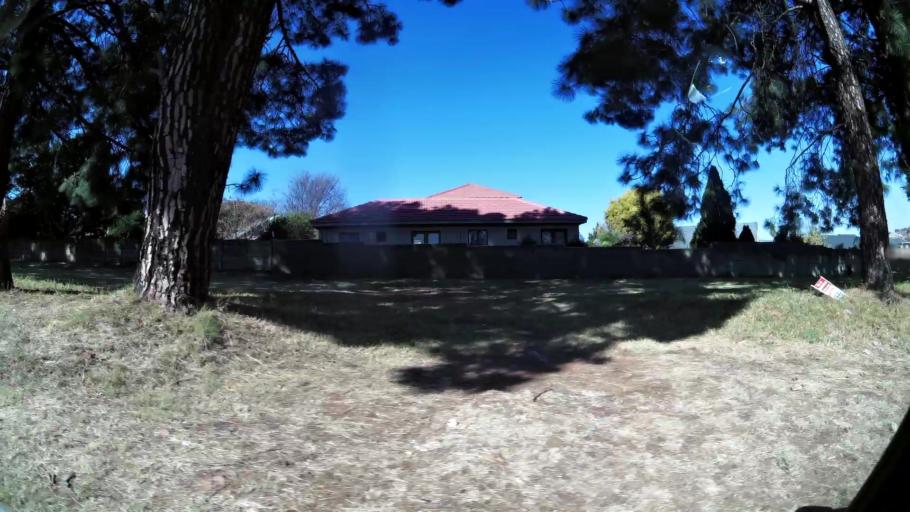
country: ZA
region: Gauteng
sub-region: City of Johannesburg Metropolitan Municipality
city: Roodepoort
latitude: -26.1258
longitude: 27.9202
